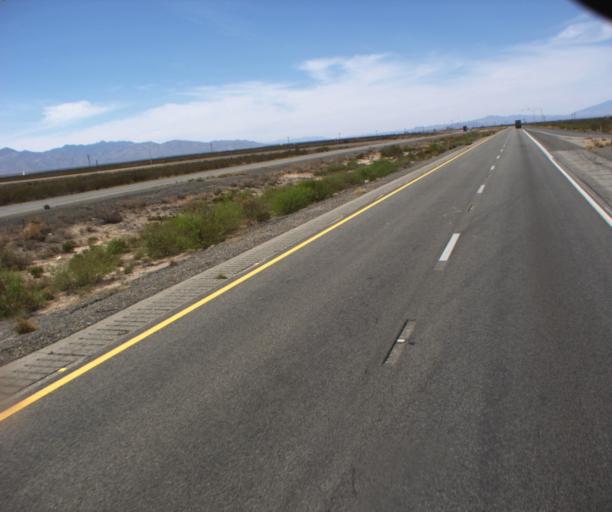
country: US
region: New Mexico
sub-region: Hidalgo County
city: Lordsburg
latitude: 32.2723
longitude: -109.2502
